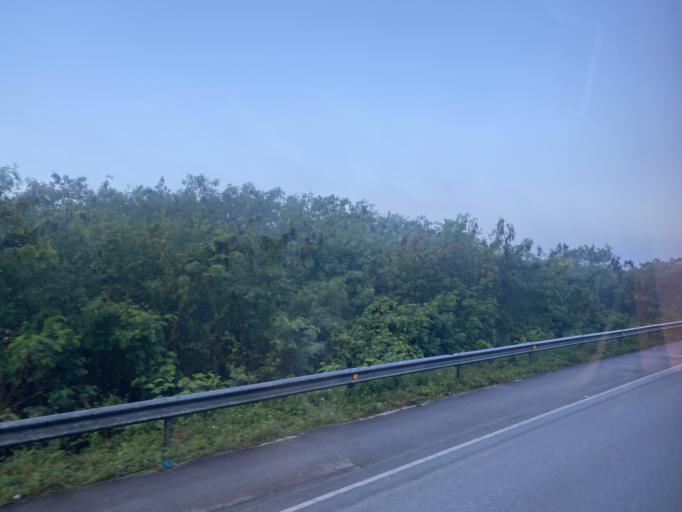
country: DO
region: La Altagracia
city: Otra Banda
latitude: 18.7334
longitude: -68.5067
